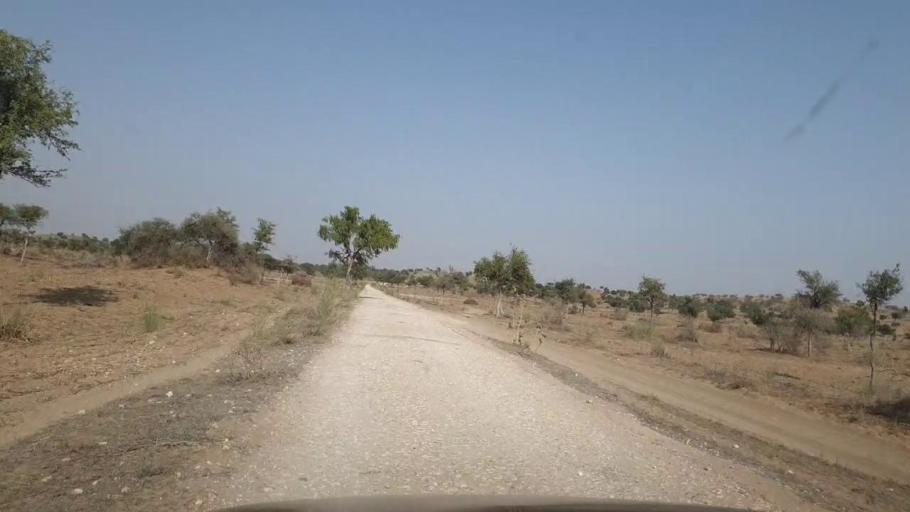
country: PK
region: Sindh
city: Islamkot
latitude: 25.1041
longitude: 70.4140
